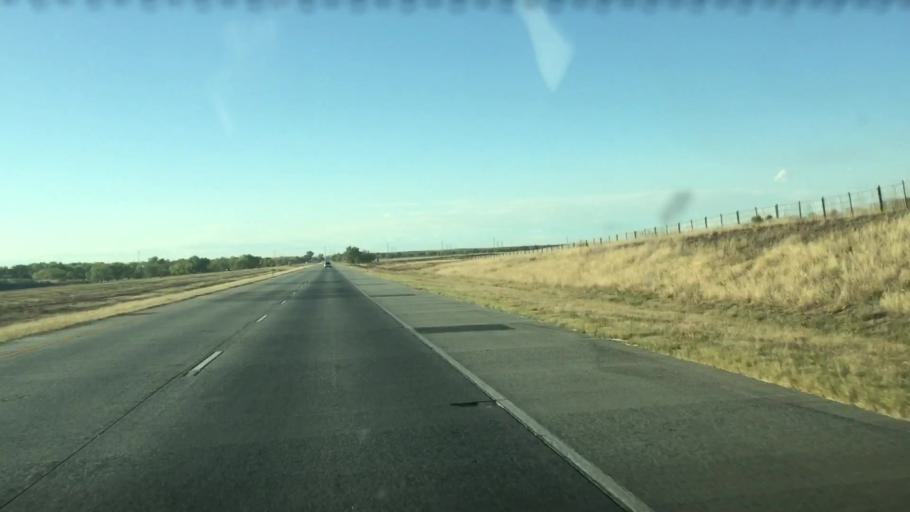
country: US
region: Colorado
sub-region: Arapahoe County
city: Byers
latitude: 39.6397
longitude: -104.0609
